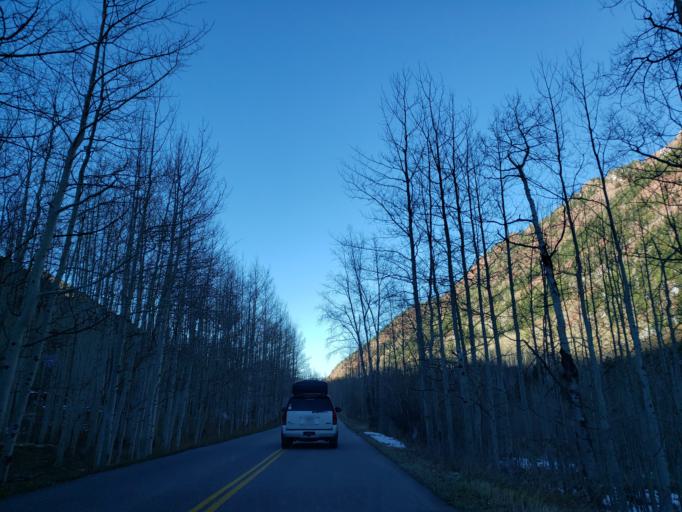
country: US
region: Colorado
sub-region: Pitkin County
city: Snowmass Village
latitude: 39.1278
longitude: -106.9036
